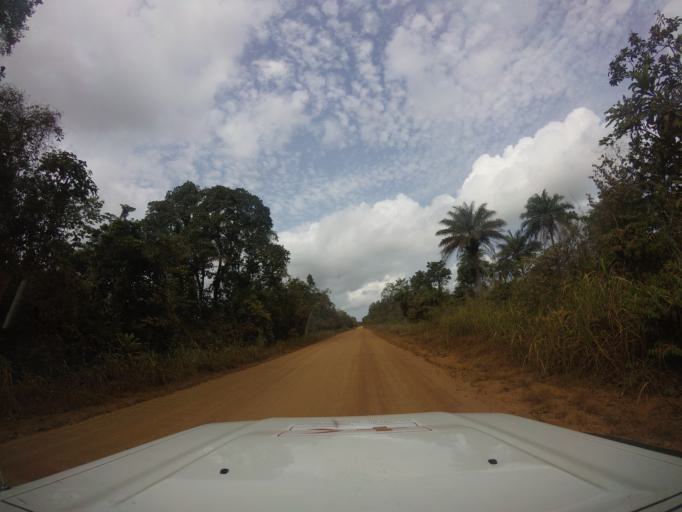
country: LR
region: Grand Cape Mount
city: Robertsport
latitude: 6.6829
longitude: -11.1293
